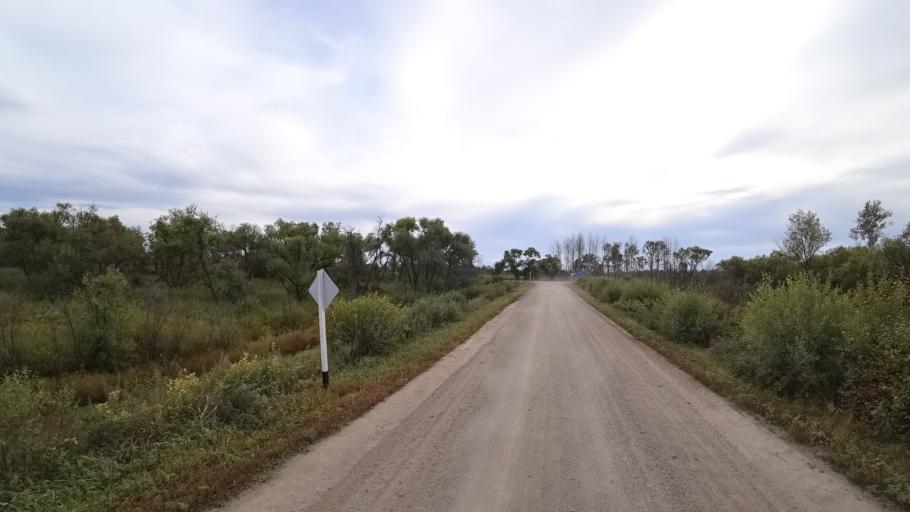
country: RU
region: Amur
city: Arkhara
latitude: 49.3740
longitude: 130.2061
